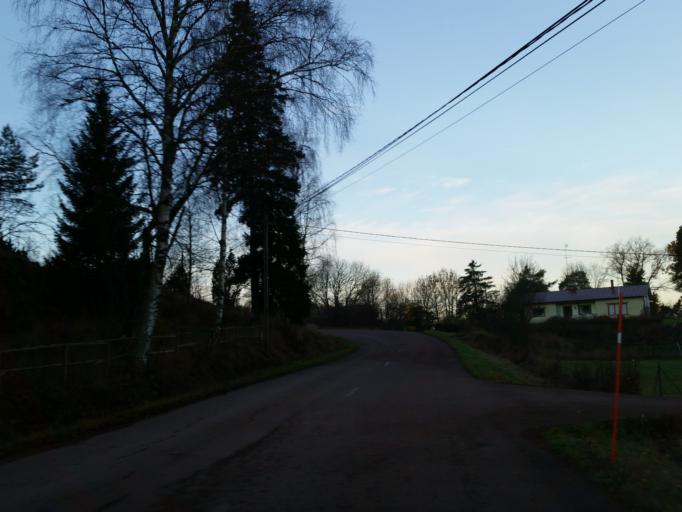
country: AX
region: Alands landsbygd
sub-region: Sund
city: Sund
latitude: 60.2089
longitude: 20.0874
